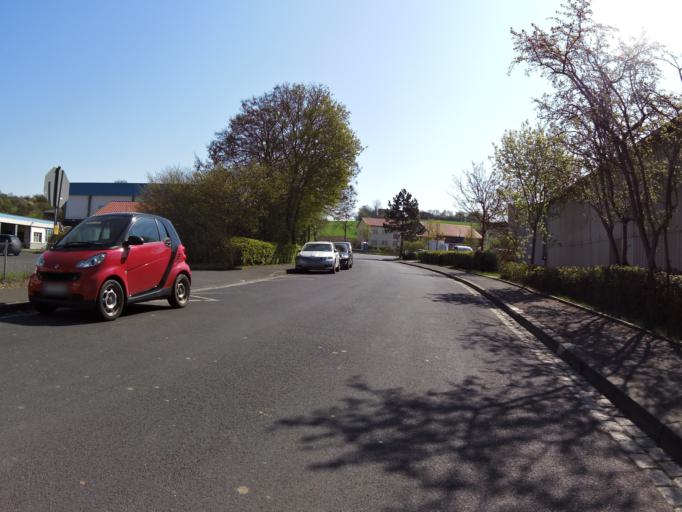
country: DE
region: Bavaria
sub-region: Regierungsbezirk Unterfranken
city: Rottendorf
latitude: 49.7903
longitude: 10.0352
